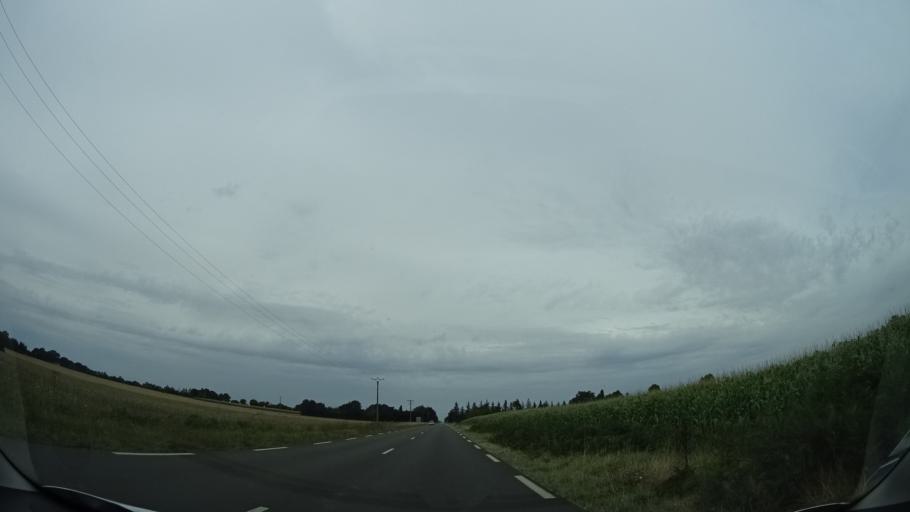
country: FR
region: Pays de la Loire
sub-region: Departement de la Mayenne
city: Meslay-du-Maine
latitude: 47.9612
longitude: -0.5737
